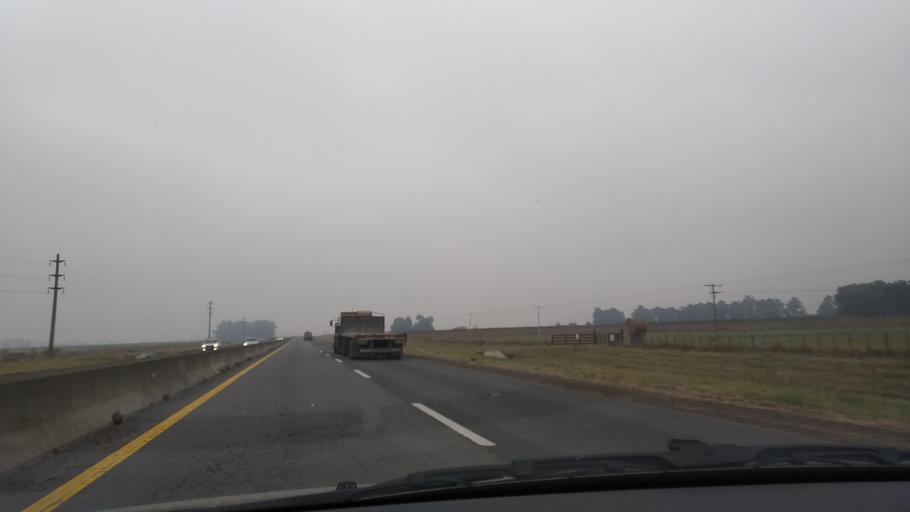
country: AR
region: Buenos Aires
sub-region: Partido de Azul
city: Azul
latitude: -36.8557
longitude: -60.0539
